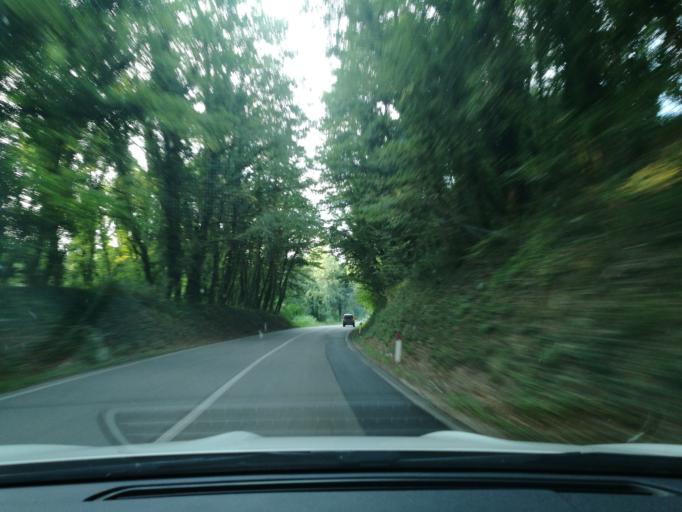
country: IT
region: Umbria
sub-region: Provincia di Terni
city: San Gemini
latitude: 42.6505
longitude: 12.5363
